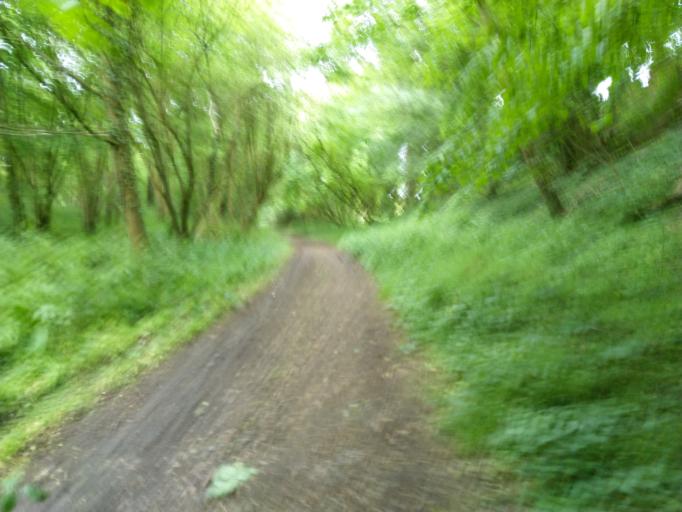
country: FR
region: Picardie
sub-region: Departement de l'Aisne
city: Guise
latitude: 49.9245
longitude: 3.5892
